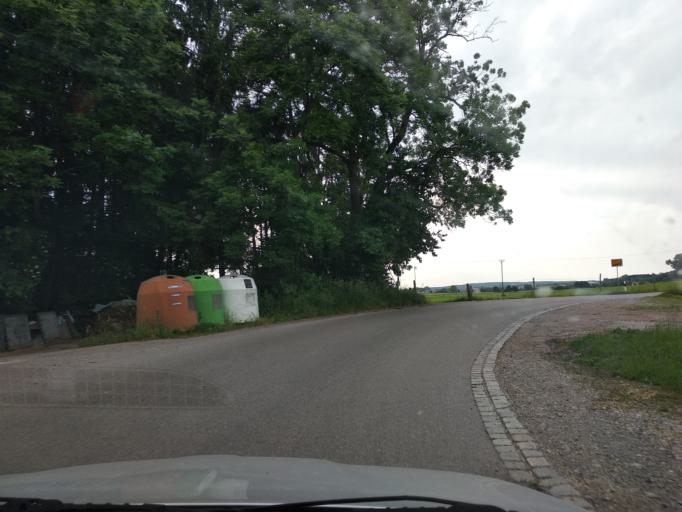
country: DE
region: Bavaria
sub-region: Swabia
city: Lachen
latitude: 47.9485
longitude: 10.2215
